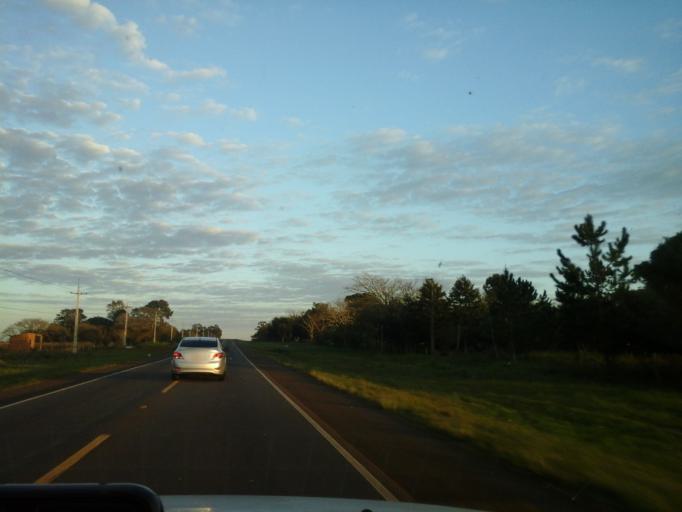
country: PY
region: Misiones
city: San Patricio
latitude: -27.0330
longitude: -56.6815
